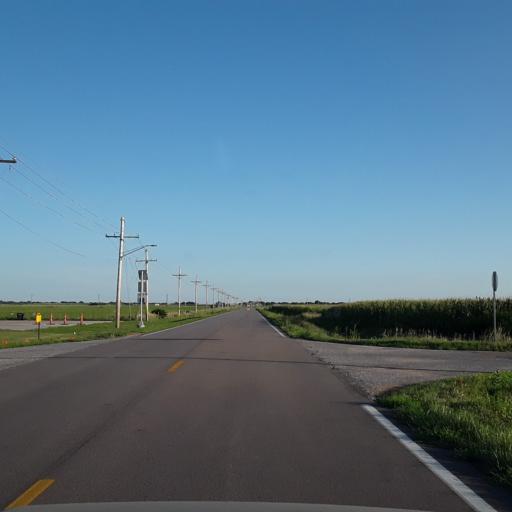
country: US
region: Nebraska
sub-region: Hall County
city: Grand Island
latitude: 40.9671
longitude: -98.3208
